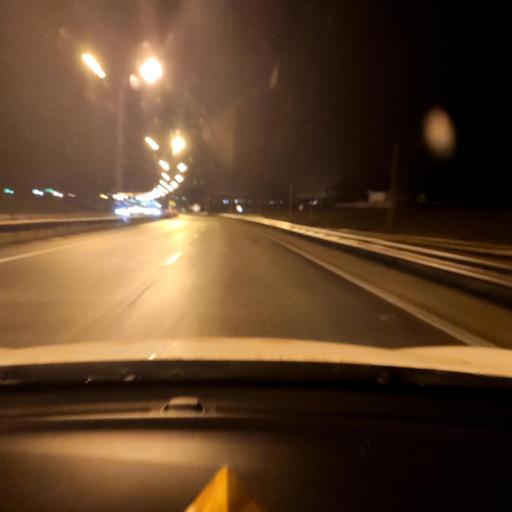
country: RU
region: Tatarstan
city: Osinovo
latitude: 55.7750
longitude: 48.8395
